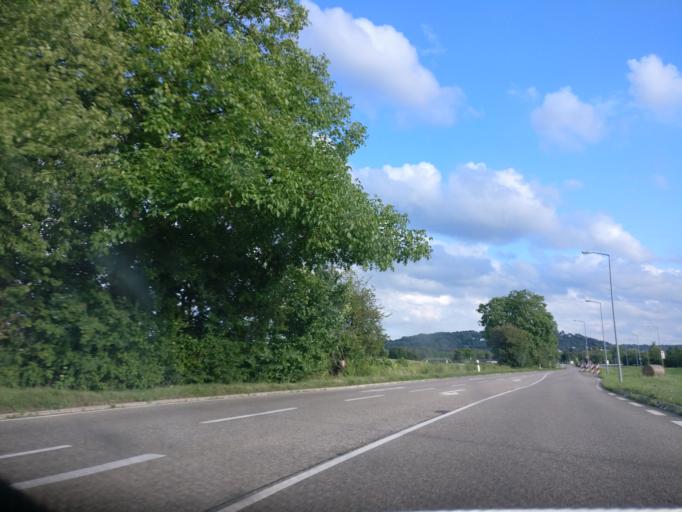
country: DE
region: Baden-Wuerttemberg
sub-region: Karlsruhe Region
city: Weingarten
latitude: 49.0194
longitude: 8.4798
